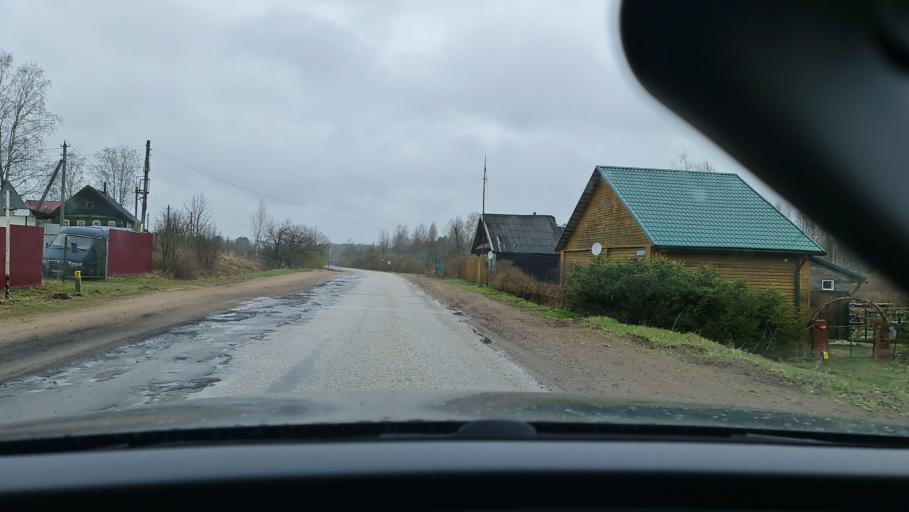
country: RU
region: Novgorod
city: Valday
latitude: 58.0369
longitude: 32.9410
